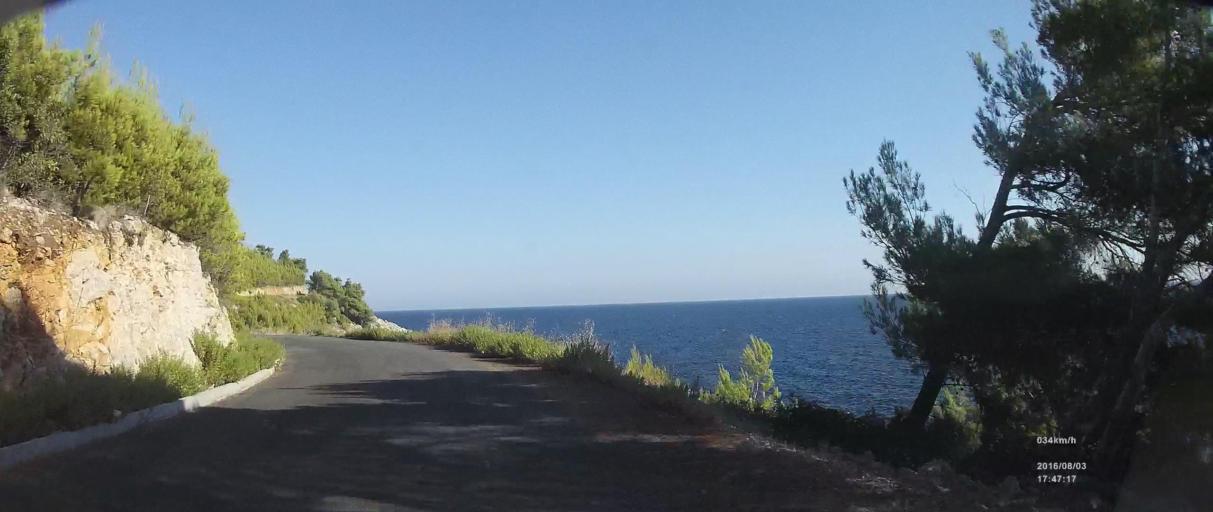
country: HR
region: Dubrovacko-Neretvanska
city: Blato
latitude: 42.7384
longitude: 17.5010
